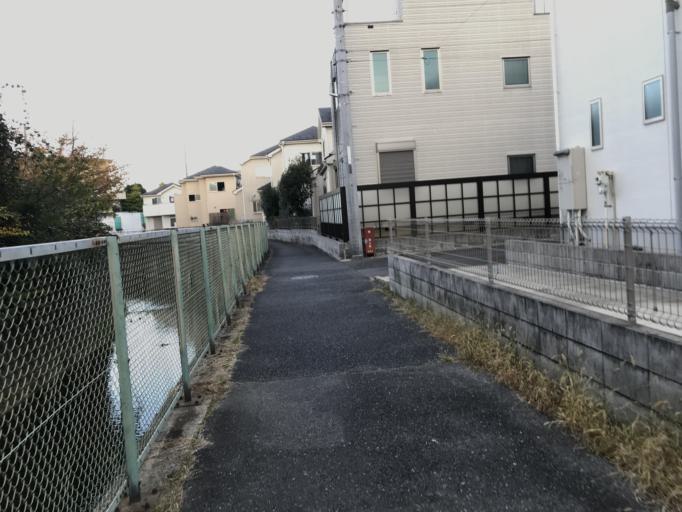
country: JP
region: Saitama
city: Wako
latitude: 35.7672
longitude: 139.6108
